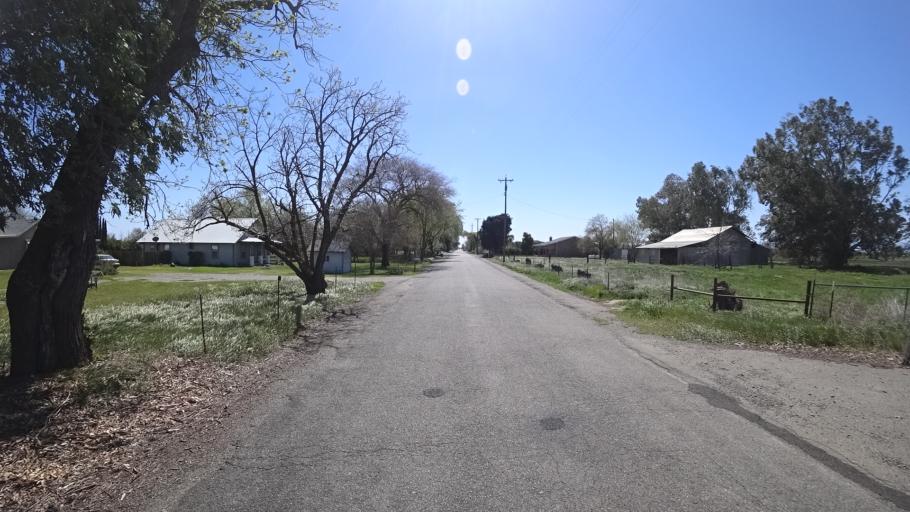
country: US
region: California
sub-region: Glenn County
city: Orland
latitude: 39.7707
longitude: -122.2296
